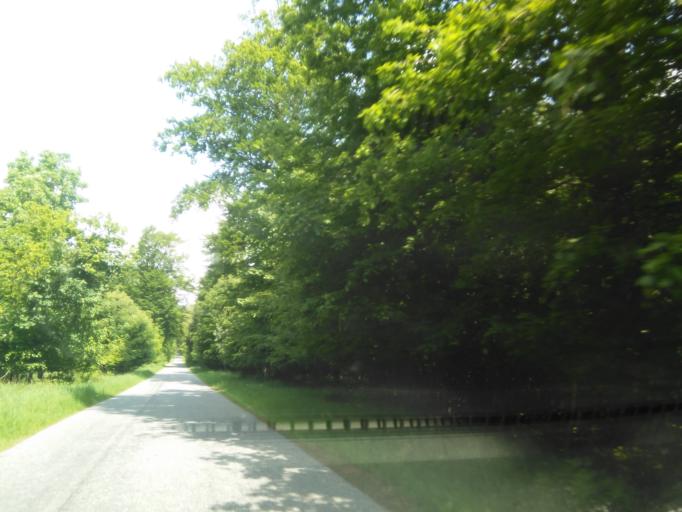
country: DK
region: Central Jutland
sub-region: Skanderborg Kommune
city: Galten
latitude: 56.2193
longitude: 9.9312
